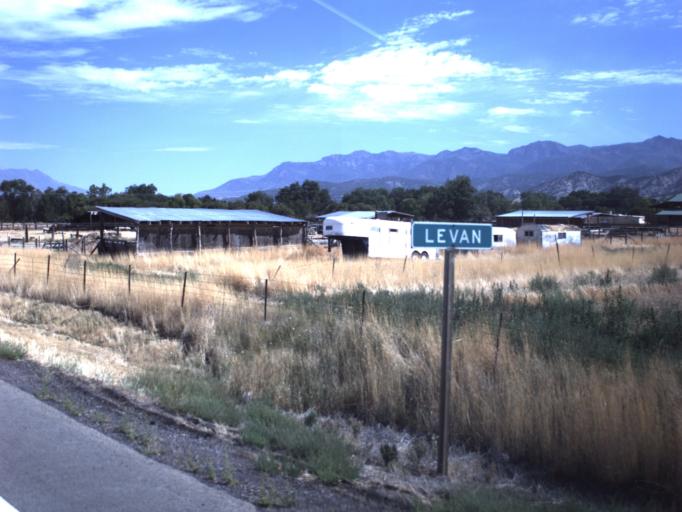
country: US
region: Utah
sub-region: Juab County
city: Nephi
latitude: 39.5494
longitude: -111.8638
